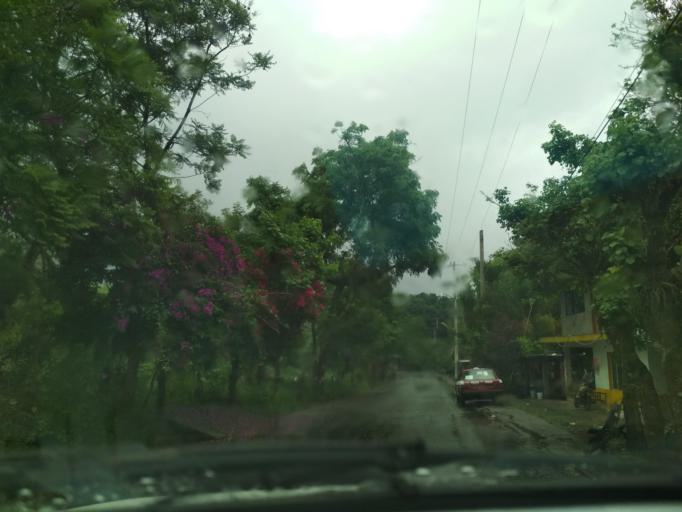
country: MX
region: Veracruz
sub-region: Mariano Escobedo
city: Chicola
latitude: 18.9016
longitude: -97.1177
